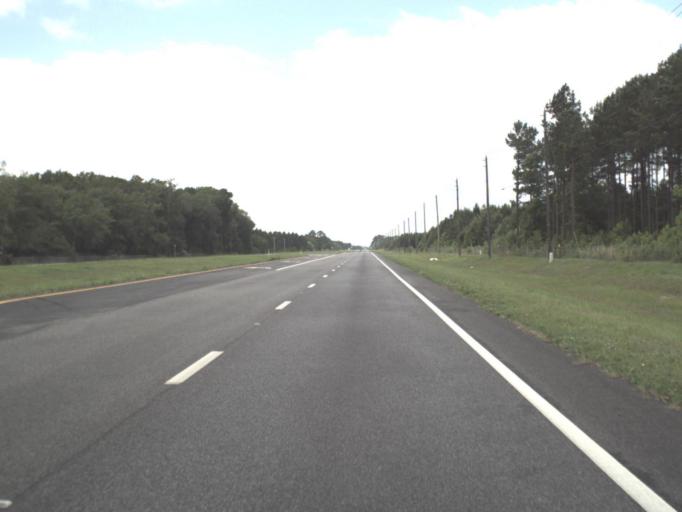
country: US
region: Florida
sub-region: Nassau County
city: Callahan
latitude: 30.6019
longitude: -81.7557
